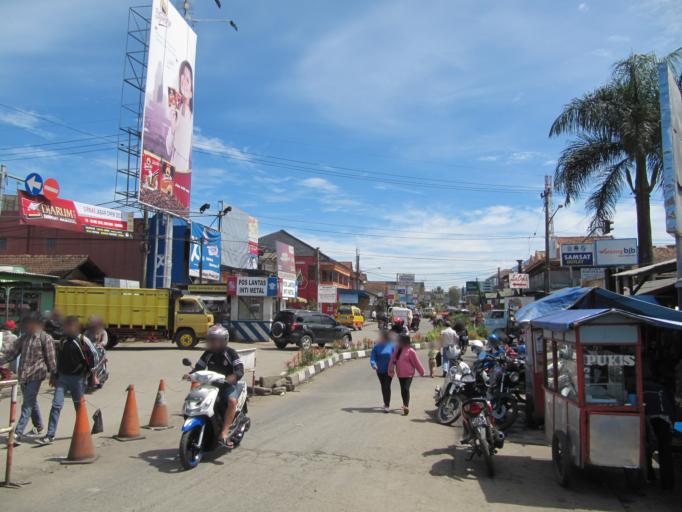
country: ID
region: West Java
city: Lembang
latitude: -6.8177
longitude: 107.6227
